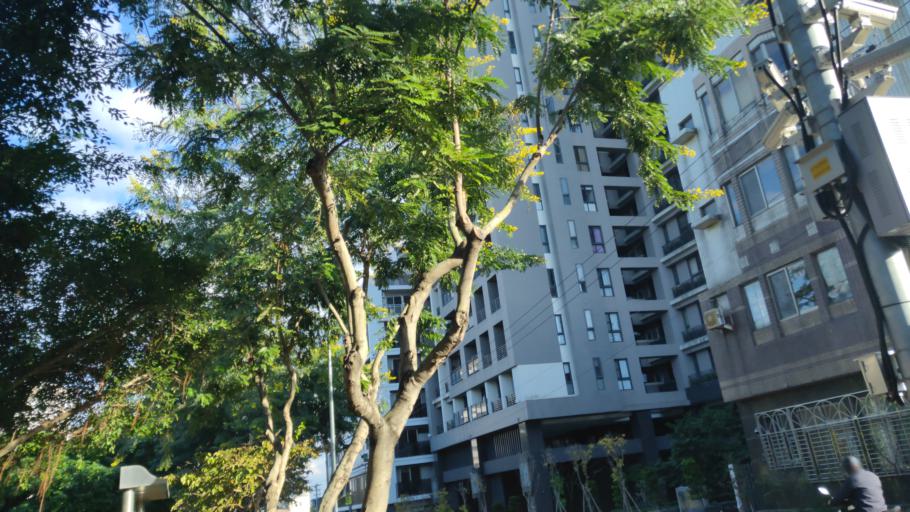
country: TW
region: Taiwan
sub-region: Taichung City
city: Taichung
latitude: 24.1405
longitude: 120.6112
